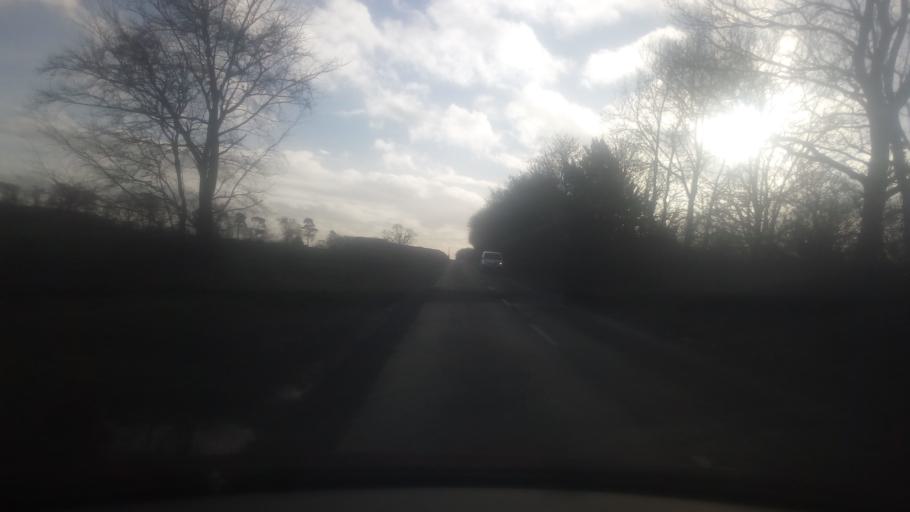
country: GB
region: Scotland
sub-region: The Scottish Borders
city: Duns
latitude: 55.6833
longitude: -2.3514
